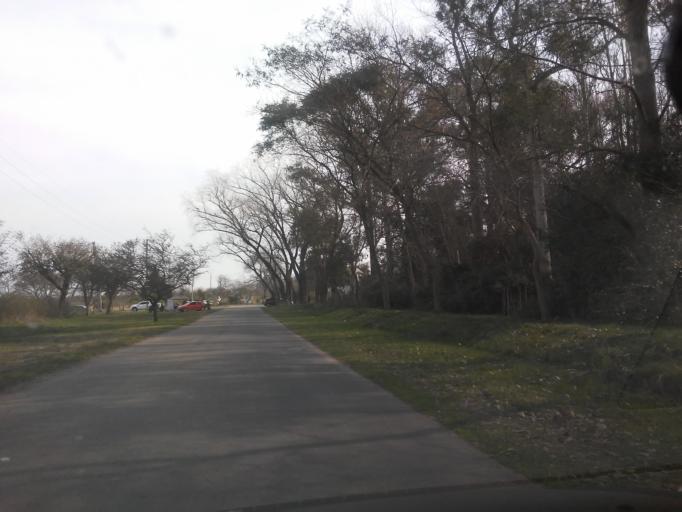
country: AR
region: Buenos Aires
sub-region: Partido de Marcos Paz
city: Marcos Paz
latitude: -34.6731
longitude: -58.8600
